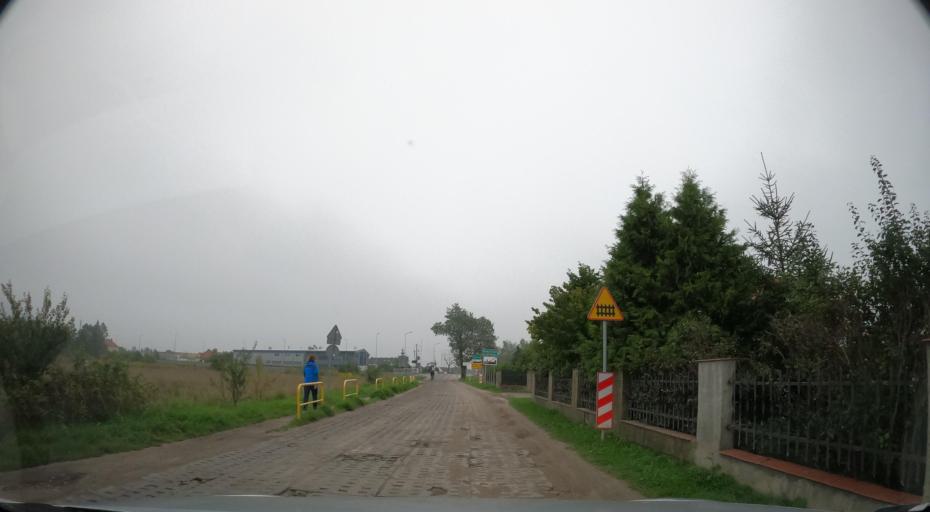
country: PL
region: Pomeranian Voivodeship
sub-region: Powiat kartuski
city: Chwaszczyno
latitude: 54.4183
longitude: 18.4474
